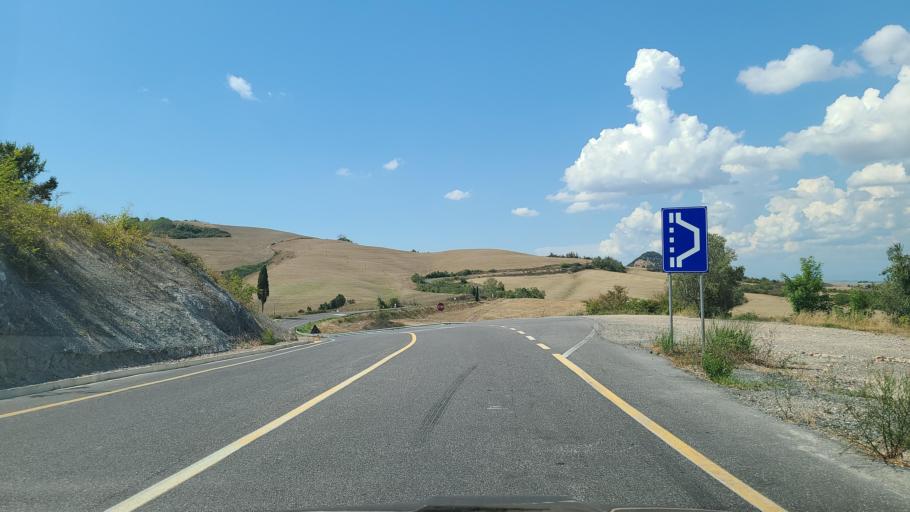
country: IT
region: Tuscany
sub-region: Province of Pisa
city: Volterra
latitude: 43.3826
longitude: 10.9261
